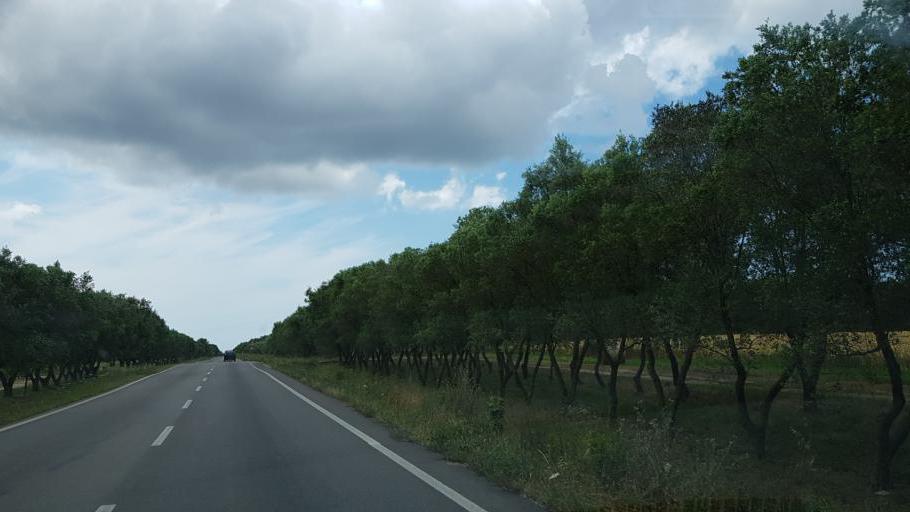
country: IT
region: Apulia
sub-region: Provincia di Brindisi
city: San Pancrazio Salentino
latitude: 40.3657
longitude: 17.8410
